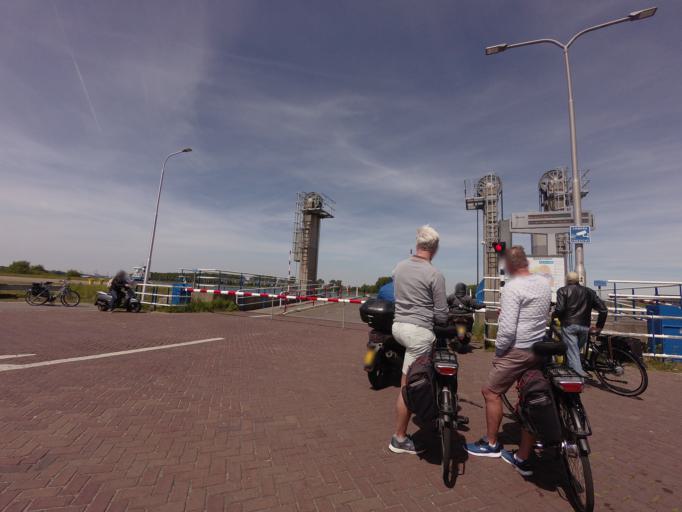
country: NL
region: North Holland
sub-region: Gemeente Velsen
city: Velsen-Zuid
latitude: 52.4313
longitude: 4.7245
